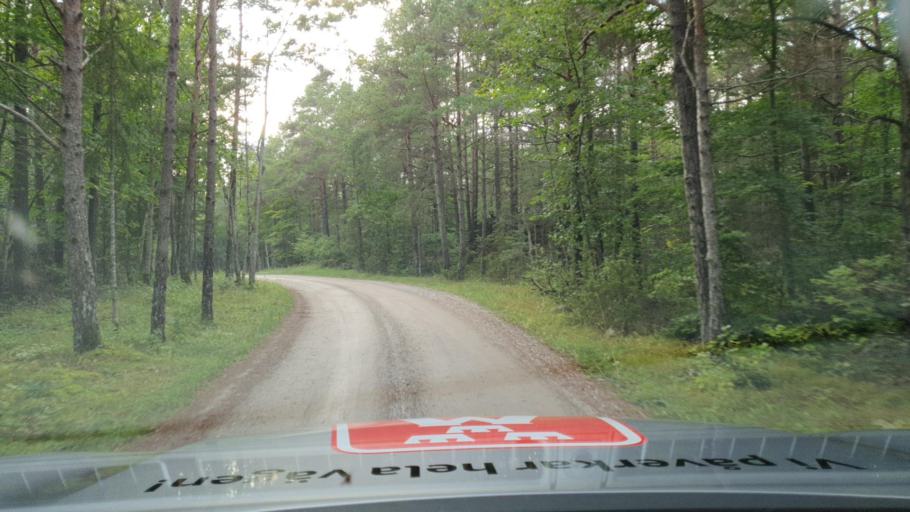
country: SE
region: Gotland
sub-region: Gotland
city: Klintehamn
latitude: 57.3790
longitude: 18.2389
